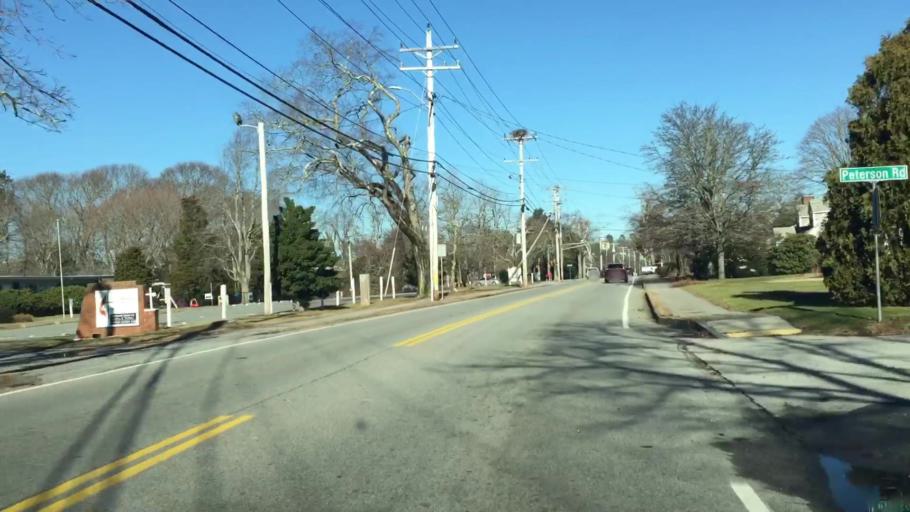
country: US
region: Massachusetts
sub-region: Barnstable County
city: Falmouth
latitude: 41.5593
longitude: -70.6108
